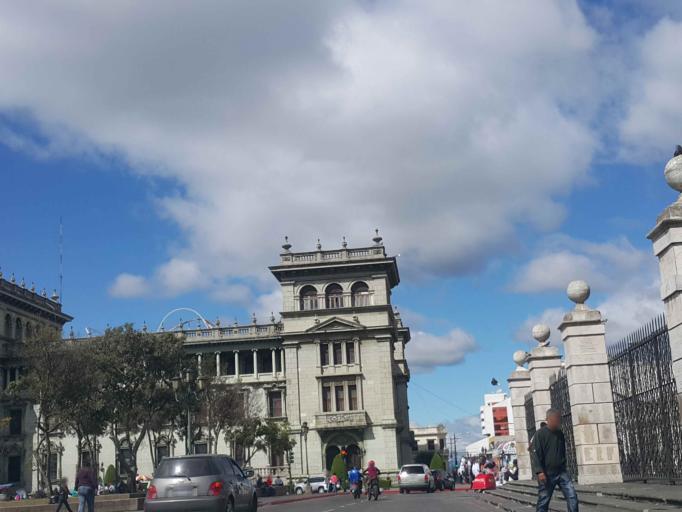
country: GT
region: Guatemala
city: Guatemala City
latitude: 14.6415
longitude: -90.5127
